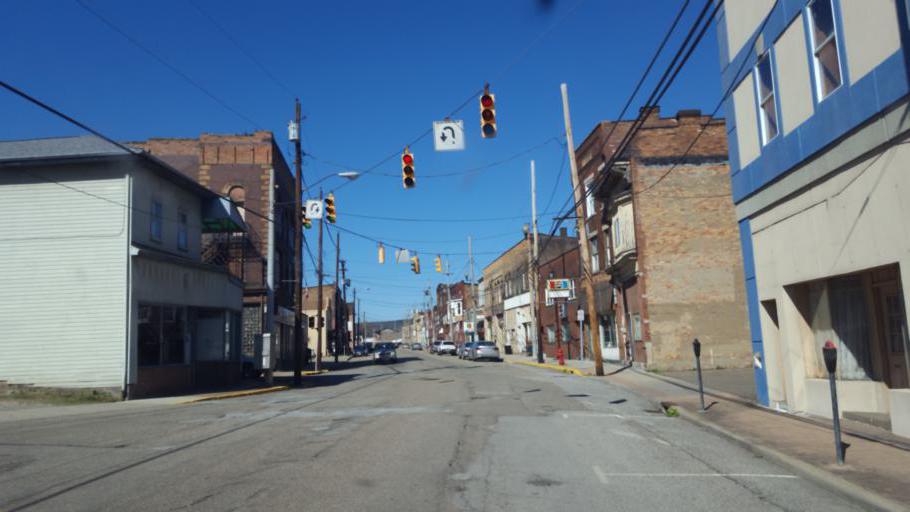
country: US
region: Ohio
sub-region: Jefferson County
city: Mingo Junction
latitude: 40.3194
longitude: -80.6072
